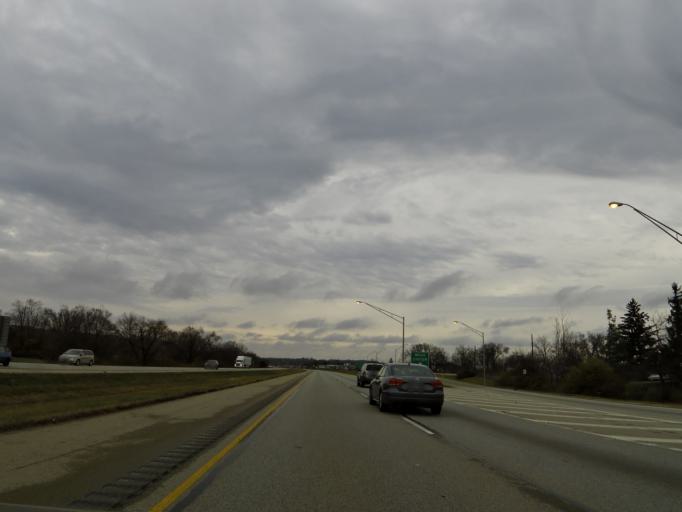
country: US
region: Ohio
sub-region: Hamilton County
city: Harrison
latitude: 39.2502
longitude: -84.7863
